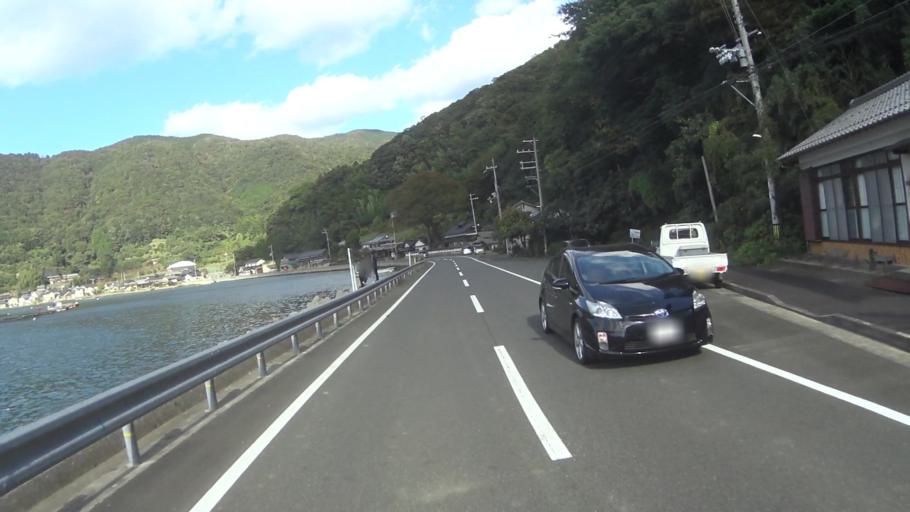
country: JP
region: Kyoto
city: Maizuru
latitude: 35.5164
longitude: 135.3493
